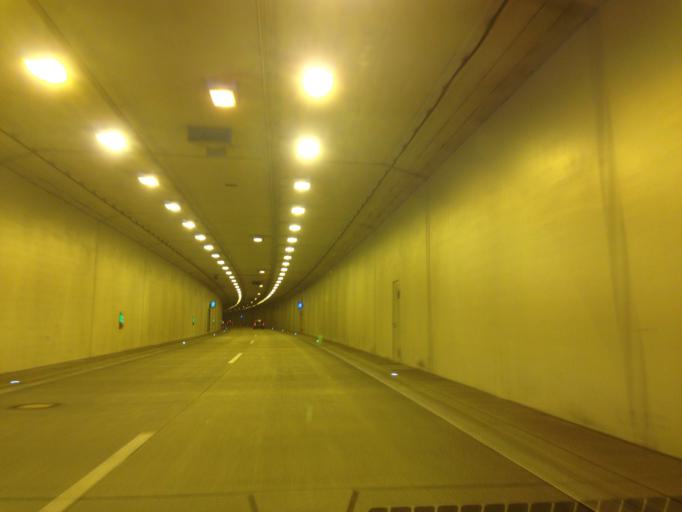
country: DE
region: Bavaria
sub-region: Swabia
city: Hopferau
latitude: 47.5992
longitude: 10.6567
